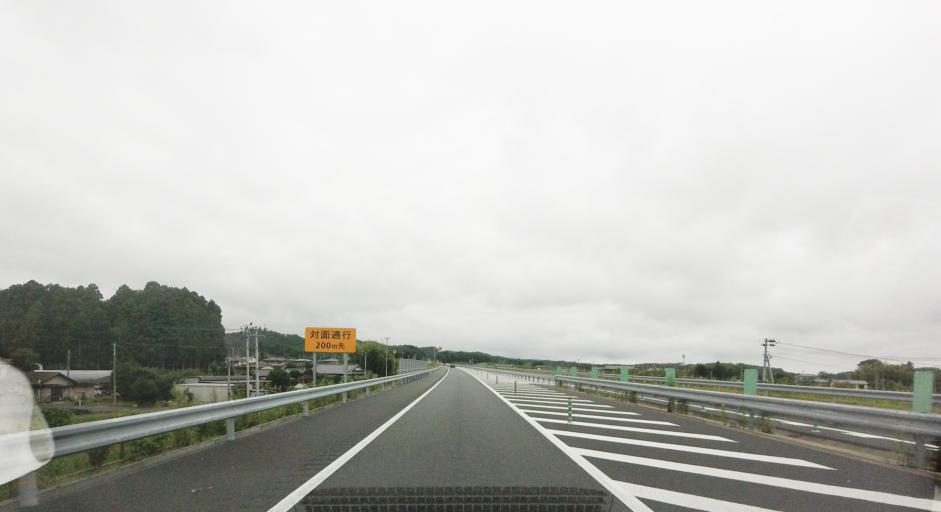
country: JP
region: Fukushima
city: Namie
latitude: 37.6299
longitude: 140.9252
